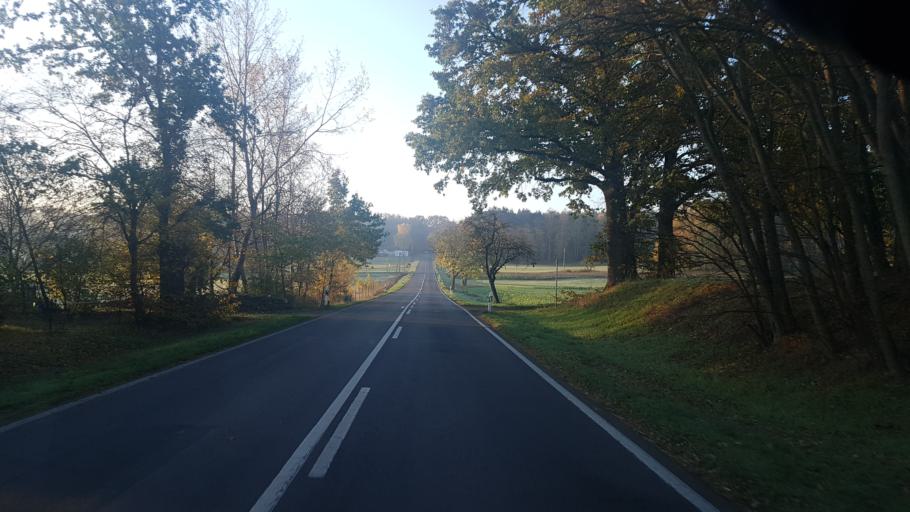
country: DE
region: Saxony
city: Schildau
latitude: 51.4307
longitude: 12.9718
